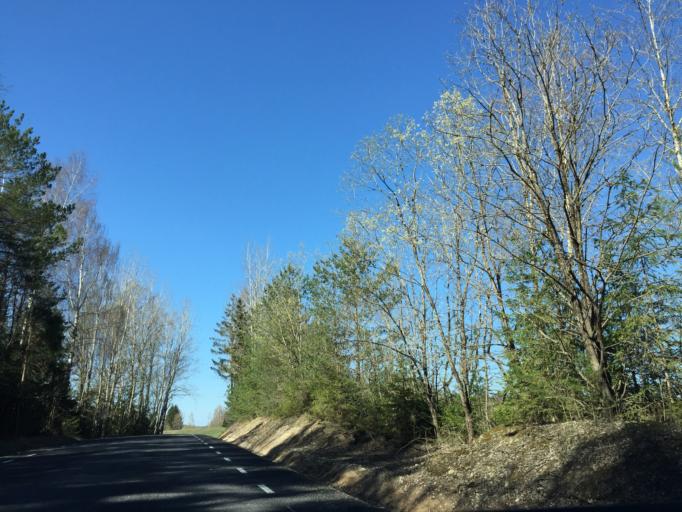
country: EE
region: Viljandimaa
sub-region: Viiratsi vald
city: Viiratsi
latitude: 58.3315
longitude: 25.7005
